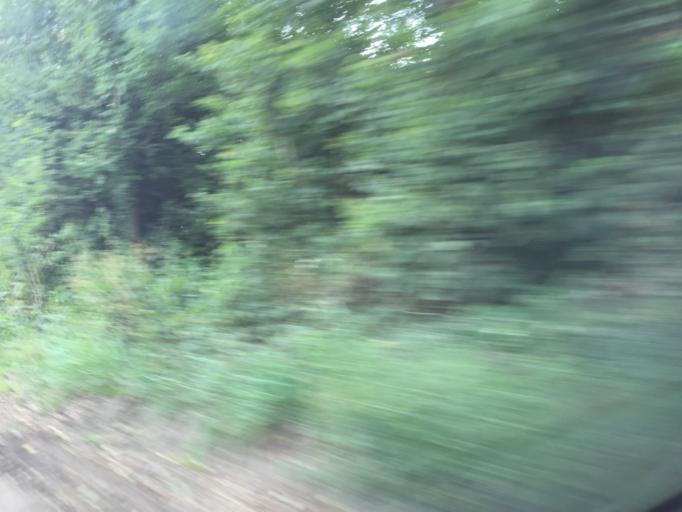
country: GB
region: England
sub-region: South Gloucestershire
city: Horton
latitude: 51.5632
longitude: -2.3520
